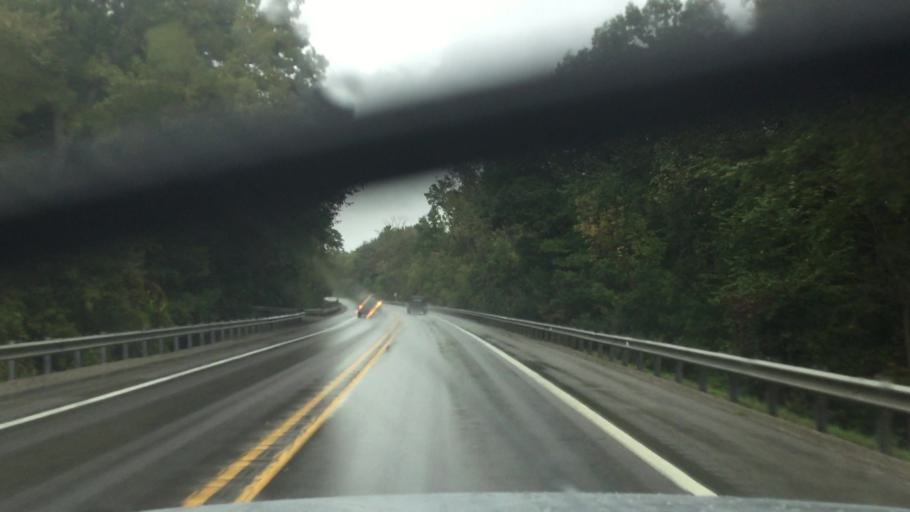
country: US
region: Michigan
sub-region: Livingston County
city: Howell
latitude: 42.6230
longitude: -83.8946
